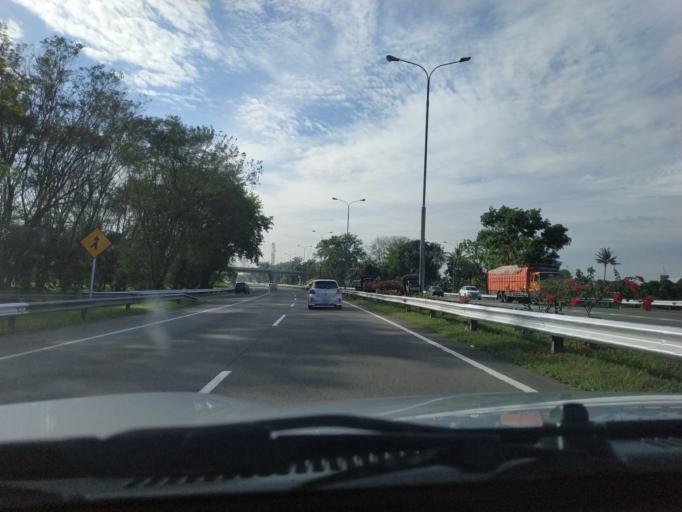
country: ID
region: North Sumatra
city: Deli Tua
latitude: 3.5452
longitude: 98.7255
